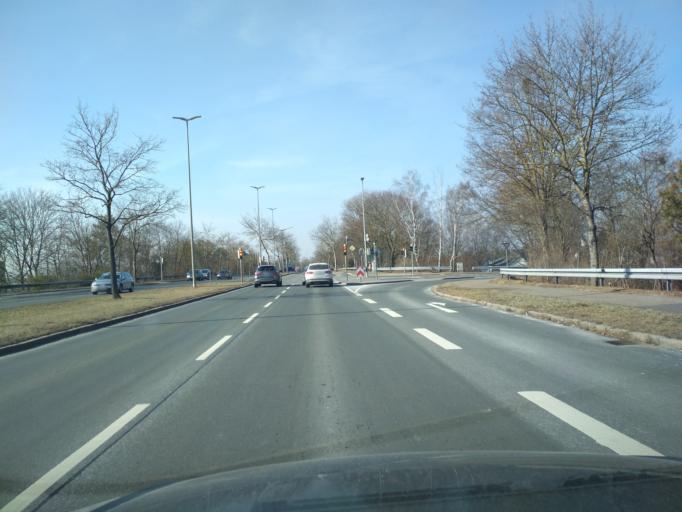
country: DE
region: Bavaria
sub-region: Regierungsbezirk Mittelfranken
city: Stein
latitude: 49.4063
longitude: 11.0591
